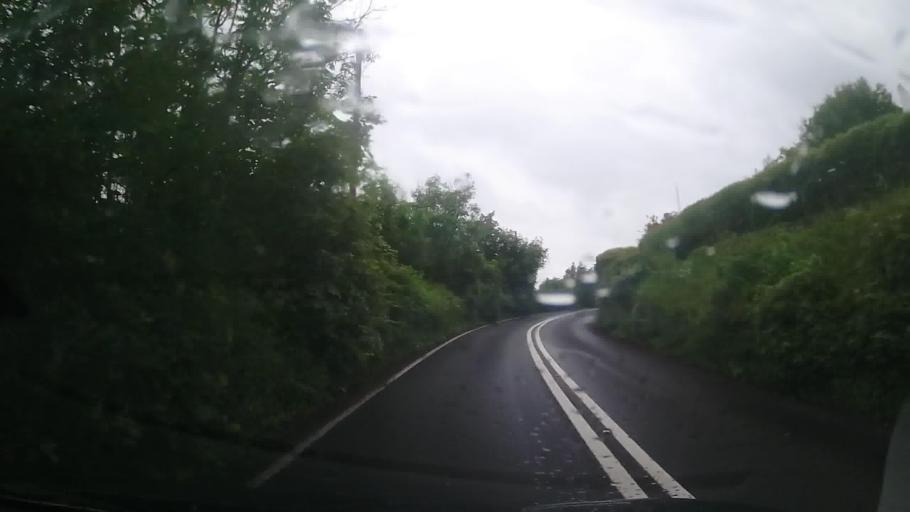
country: GB
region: England
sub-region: Devon
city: Dartmouth
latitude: 50.3628
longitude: -3.5748
